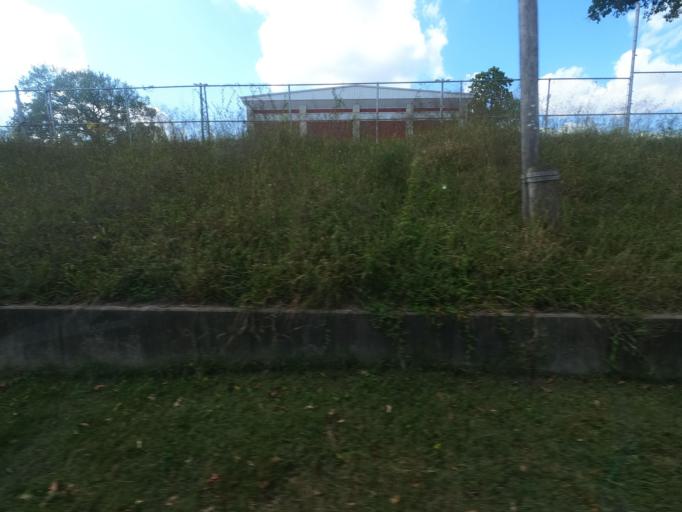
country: US
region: Illinois
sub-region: Johnson County
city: Vienna
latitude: 37.4177
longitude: -88.8933
